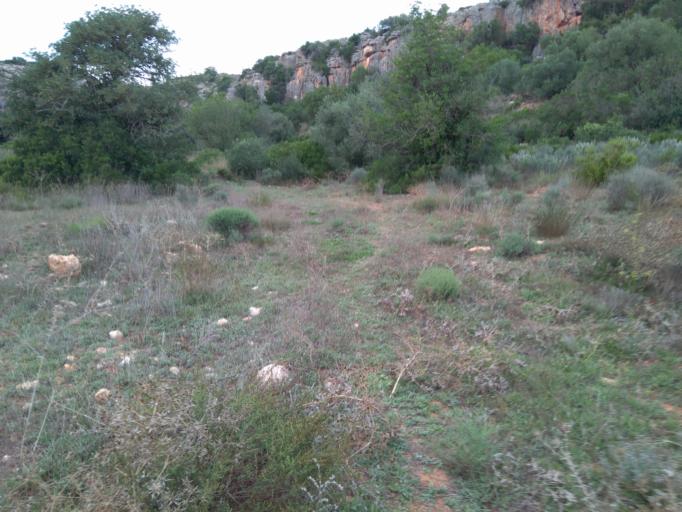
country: ES
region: Valencia
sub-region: Provincia de Valencia
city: Benimodo
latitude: 39.1983
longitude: -0.5869
